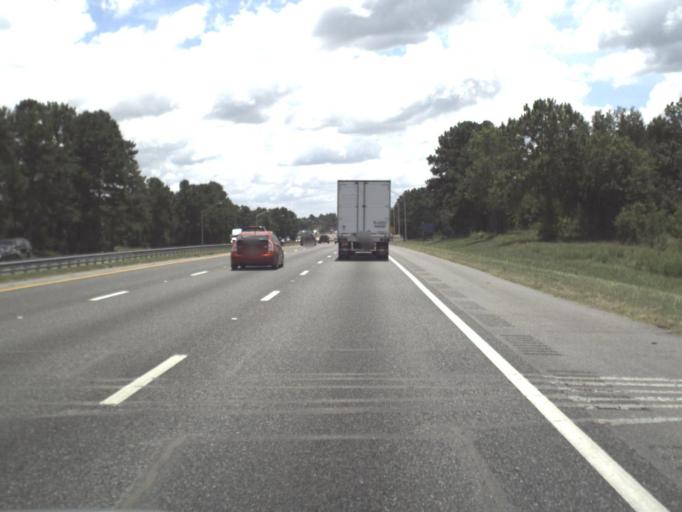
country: US
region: Florida
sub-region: Alachua County
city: High Springs
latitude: 29.9861
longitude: -82.5819
